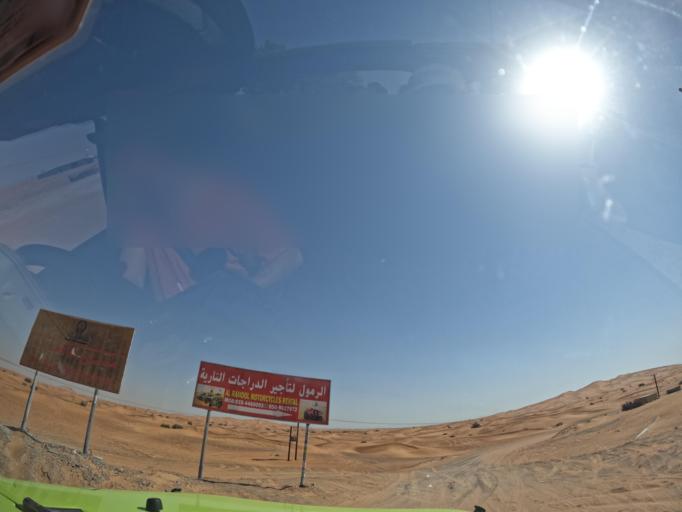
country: AE
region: Ash Shariqah
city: Adh Dhayd
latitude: 24.9652
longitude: 55.7068
